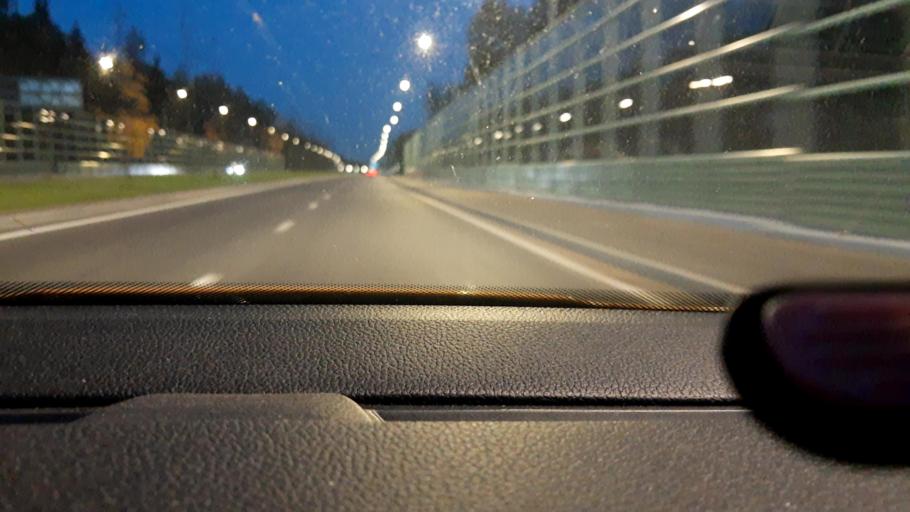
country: RU
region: Moskovskaya
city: Filimonki
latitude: 55.5715
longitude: 37.3602
